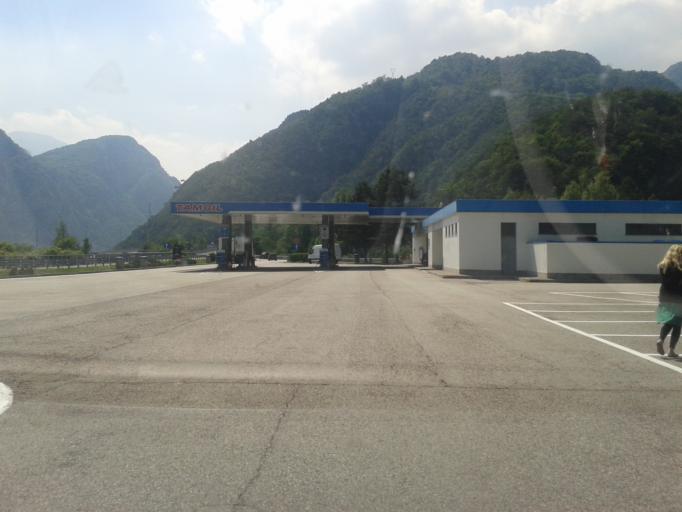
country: IT
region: Friuli Venezia Giulia
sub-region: Provincia di Udine
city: Moggio di Sotto
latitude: 46.3985
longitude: 13.1679
